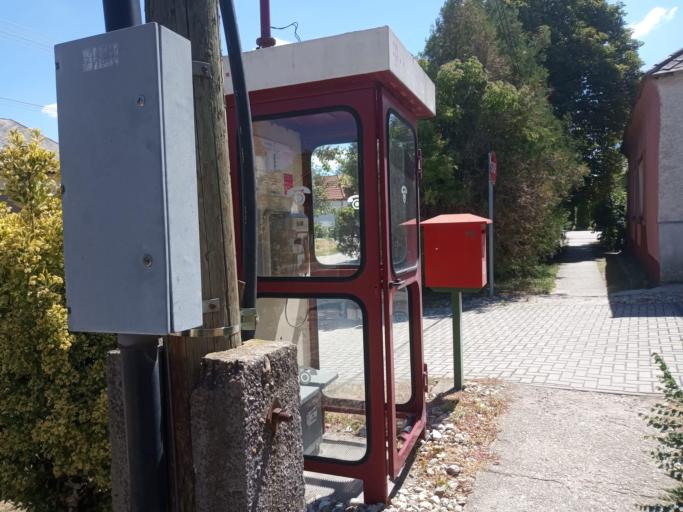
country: HU
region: Fejer
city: Kincsesbanya
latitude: 47.2441
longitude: 18.3331
